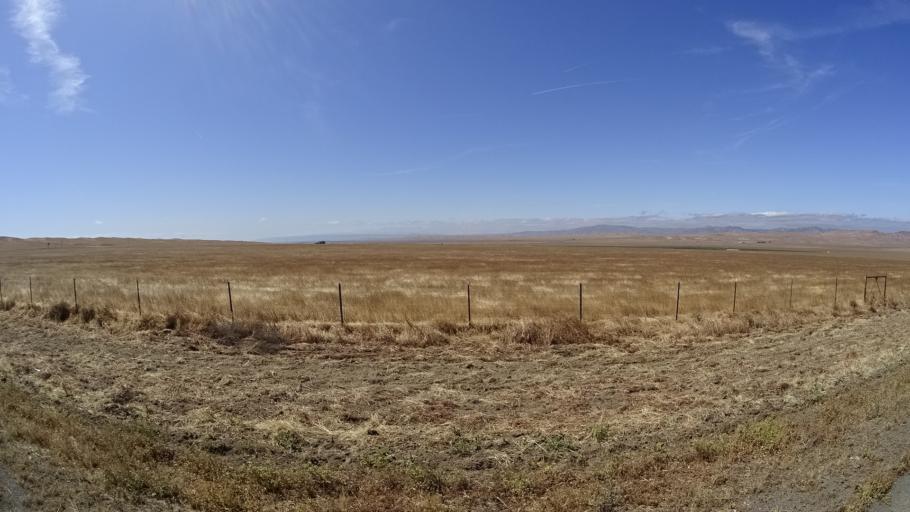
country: US
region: California
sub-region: Kings County
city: Kettleman City
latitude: 35.9353
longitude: -120.0264
